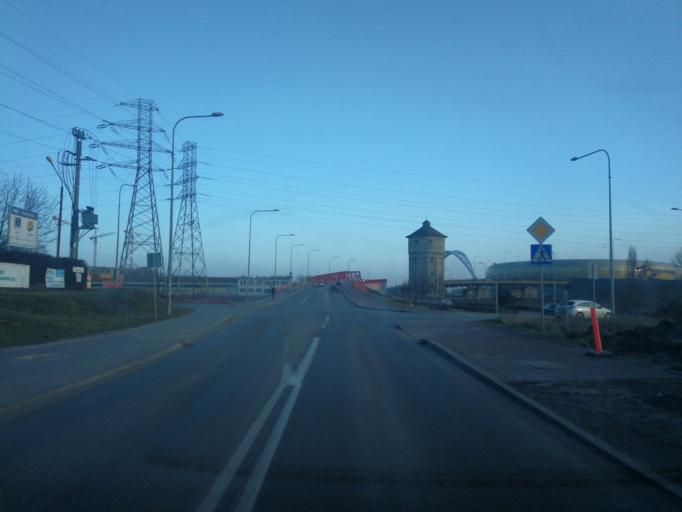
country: PL
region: Pomeranian Voivodeship
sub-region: Gdansk
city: Gdansk
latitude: 54.3963
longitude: 18.6356
